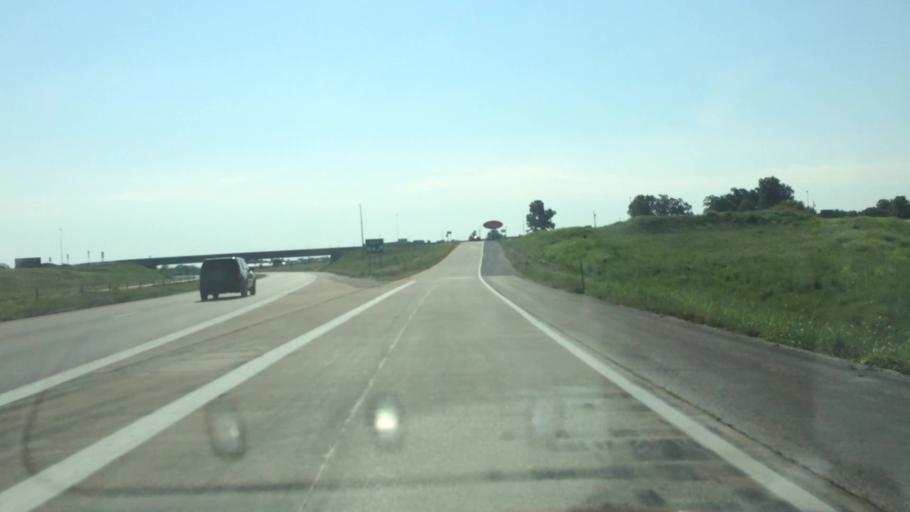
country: US
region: Missouri
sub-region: Greene County
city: Strafford
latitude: 37.2501
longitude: -93.1868
